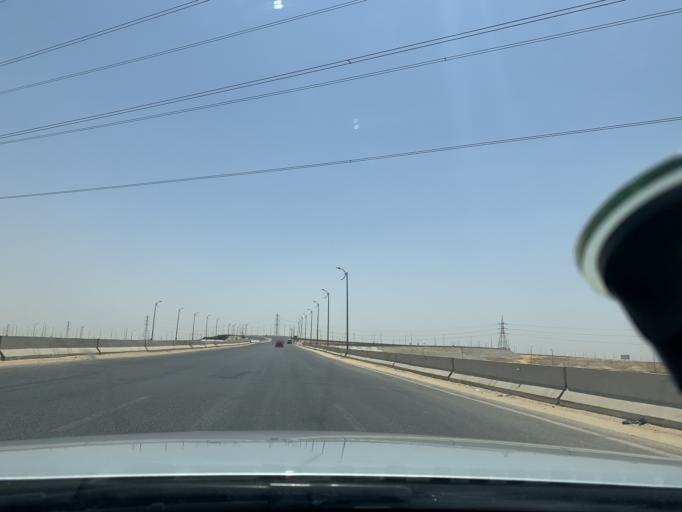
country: EG
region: Muhafazat al Qahirah
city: Halwan
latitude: 29.9725
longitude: 31.4698
